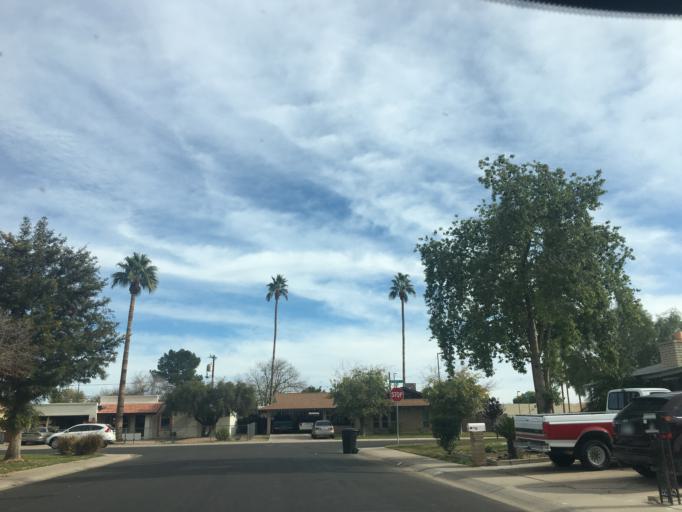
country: US
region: Arizona
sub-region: Maricopa County
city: Gilbert
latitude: 33.3467
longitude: -111.7966
